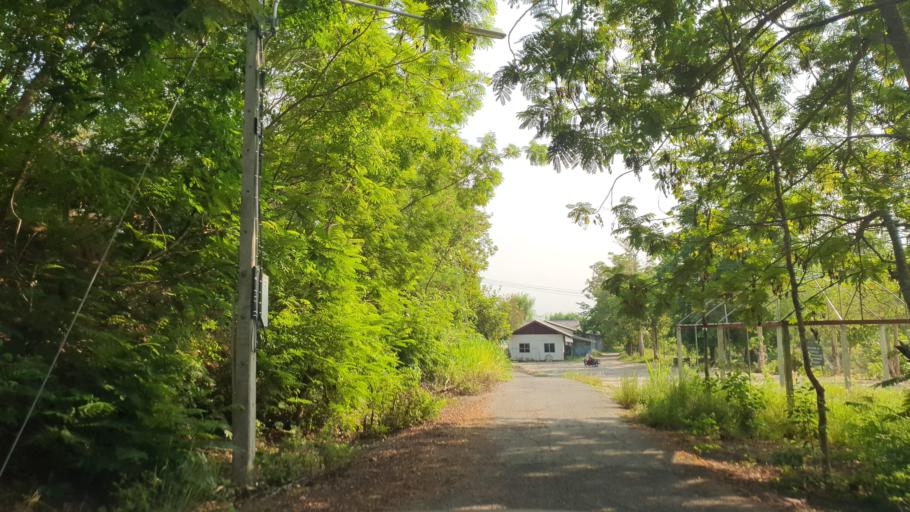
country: TH
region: Chiang Mai
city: San Pa Tong
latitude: 18.6482
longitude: 98.8420
